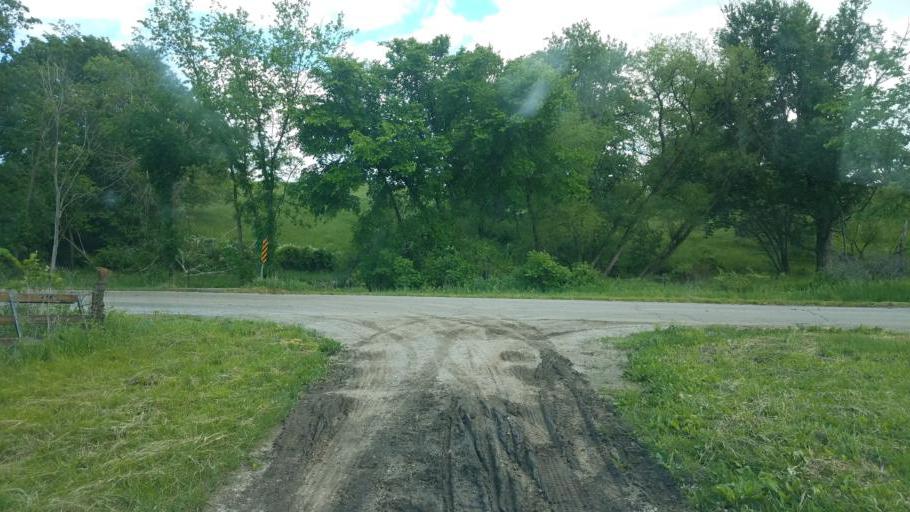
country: US
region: Missouri
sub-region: Grundy County
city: Trenton
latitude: 40.2493
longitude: -93.6865
